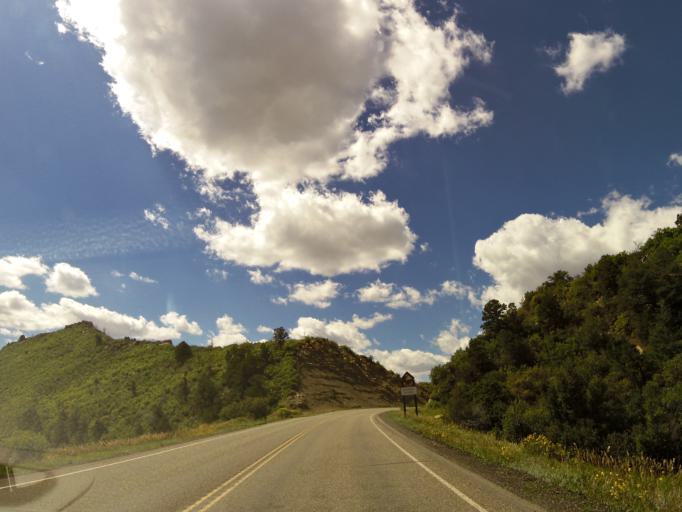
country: US
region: Colorado
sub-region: Montezuma County
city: Mancos
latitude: 37.3017
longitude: -108.4113
